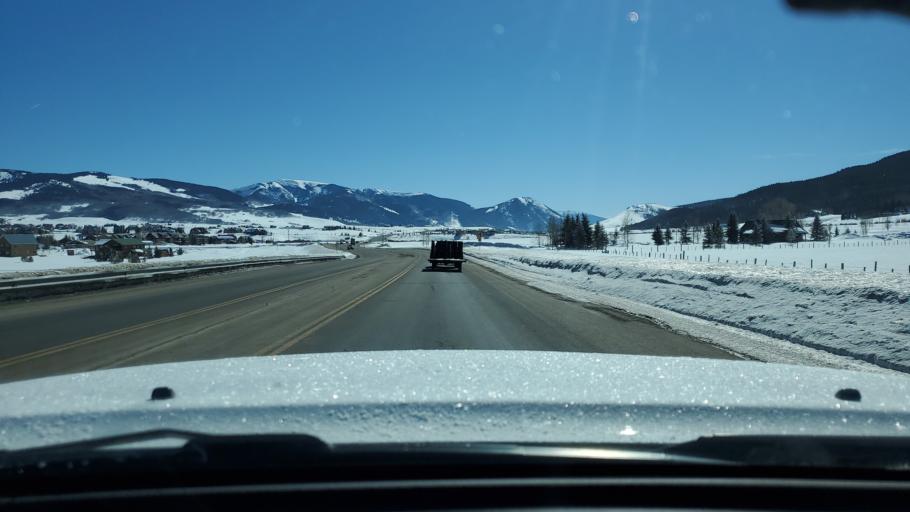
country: US
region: Colorado
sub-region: Gunnison County
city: Crested Butte
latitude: 38.8568
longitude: -106.9640
